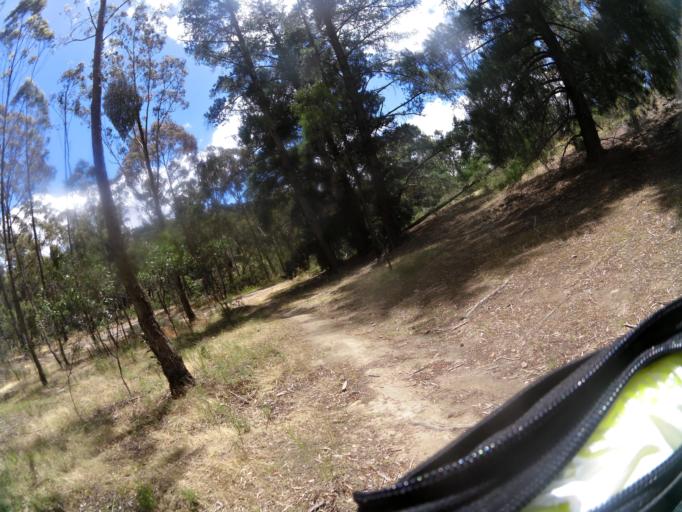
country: AU
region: Victoria
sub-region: Mount Alexander
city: Castlemaine
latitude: -37.0601
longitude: 144.2666
